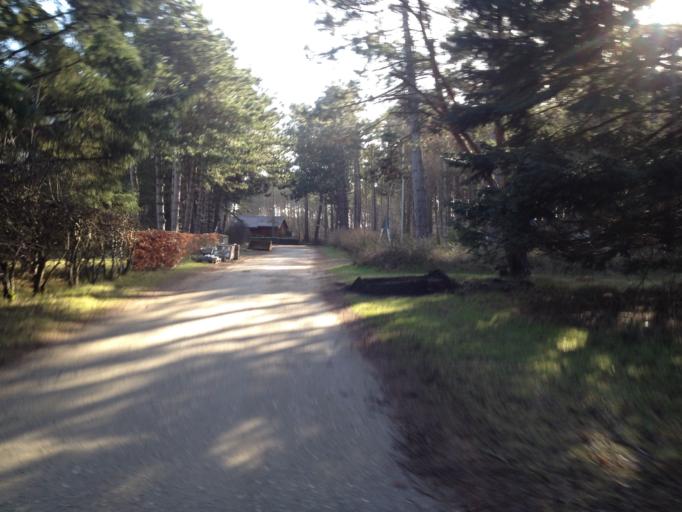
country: DE
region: Schleswig-Holstein
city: Nebel
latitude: 54.6420
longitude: 8.3486
